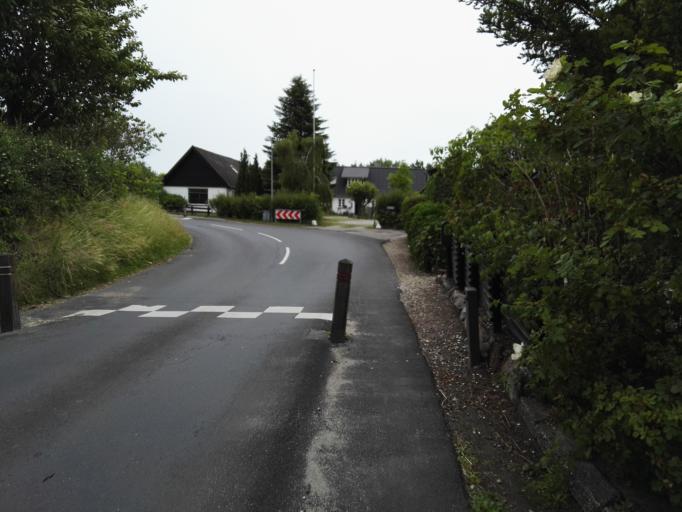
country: DK
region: Zealand
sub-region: Roskilde Kommune
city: Jyllinge
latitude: 55.7554
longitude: 12.1037
